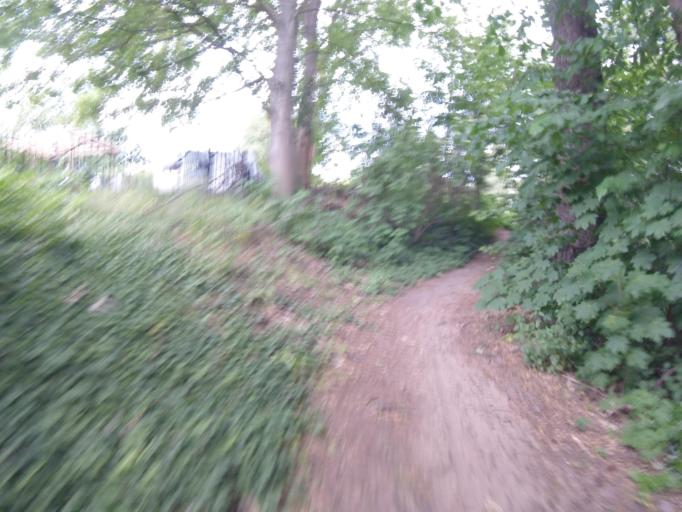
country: DE
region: Brandenburg
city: Halbe
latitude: 52.1124
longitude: 13.6922
